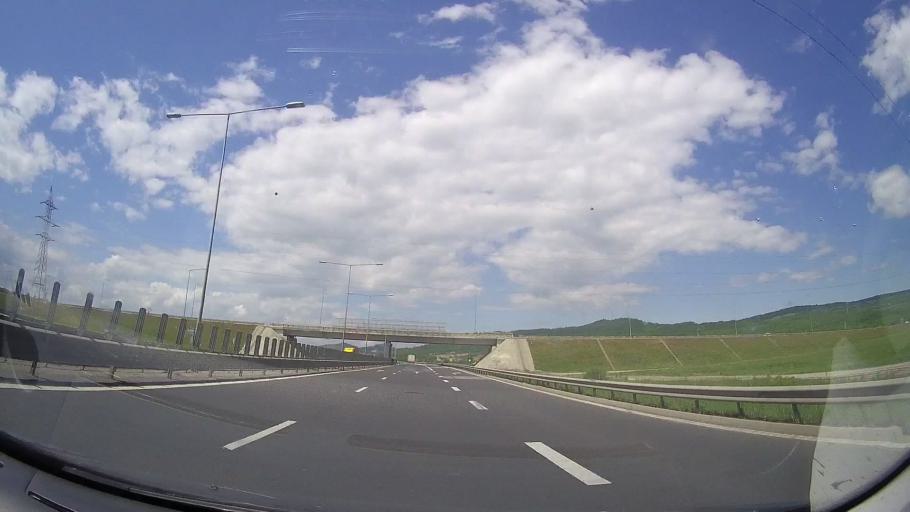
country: RO
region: Sibiu
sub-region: Comuna Selimbar
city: Selimbar
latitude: 45.7884
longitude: 24.1995
